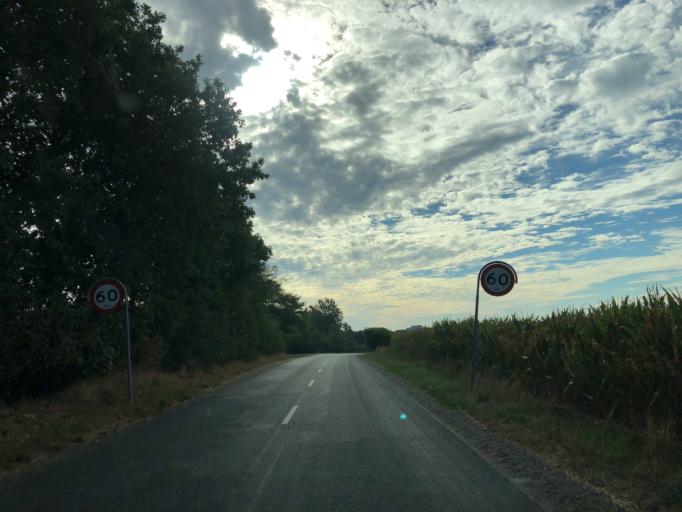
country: DK
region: Central Jutland
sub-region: Holstebro Kommune
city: Ulfborg
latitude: 56.1447
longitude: 8.4048
